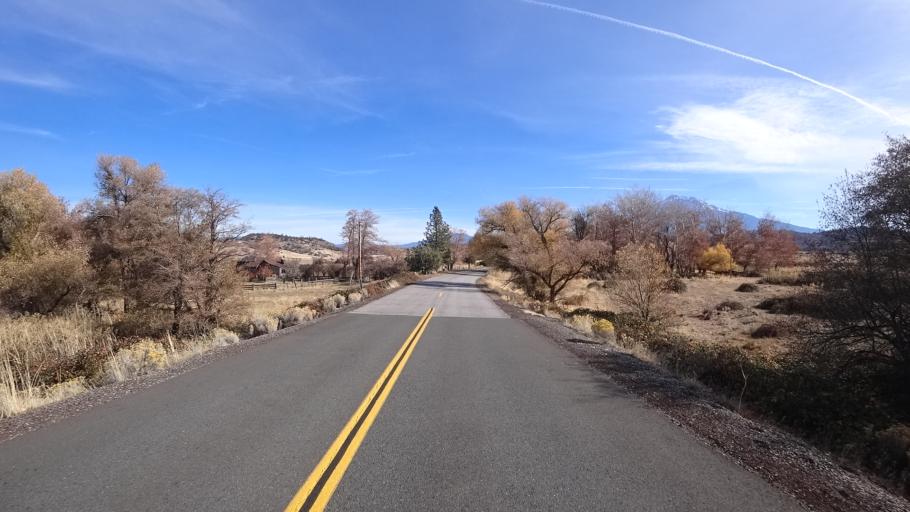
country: US
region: California
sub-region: Siskiyou County
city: Weed
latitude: 41.4708
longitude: -122.4403
